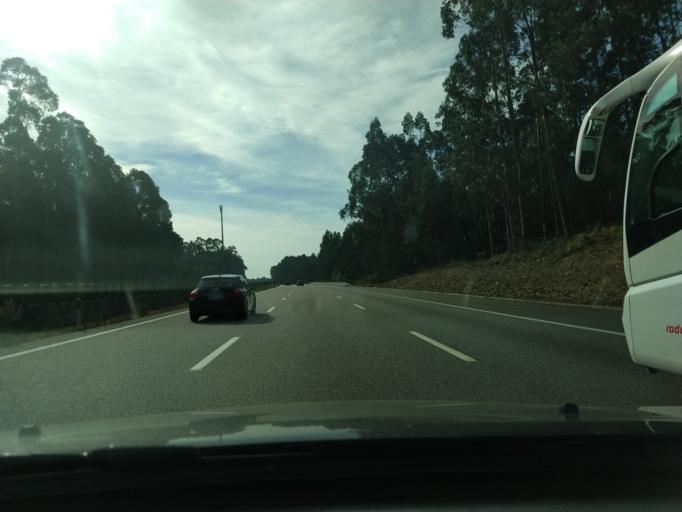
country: PT
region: Aveiro
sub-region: Estarreja
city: Avanca
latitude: 40.8264
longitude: -8.5537
